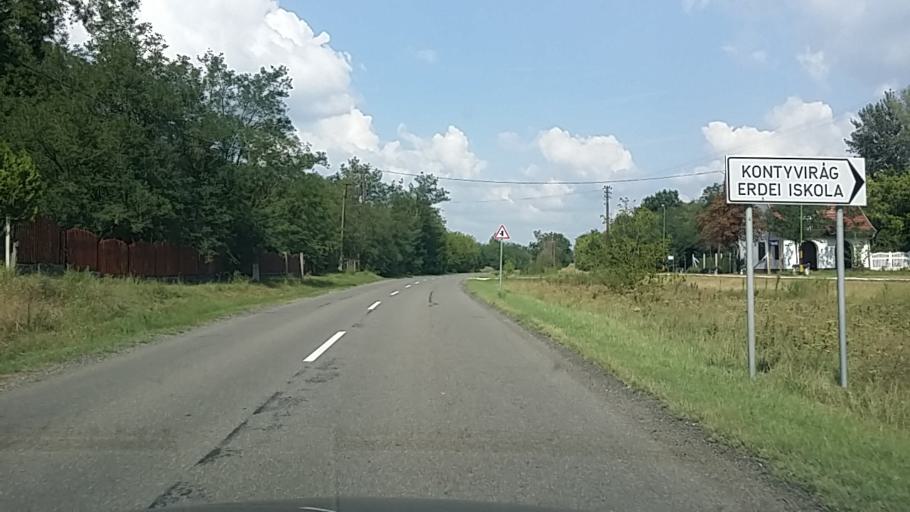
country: HU
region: Bacs-Kiskun
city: Lakitelek
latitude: 46.8506
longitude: 19.9794
